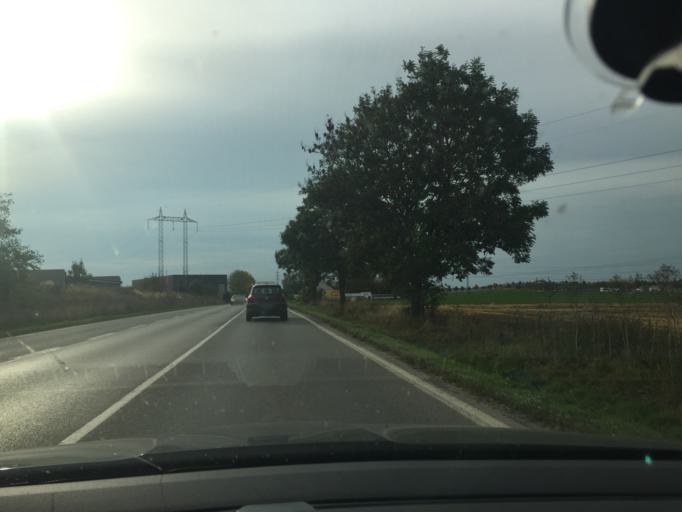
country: CZ
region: Central Bohemia
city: Sestajovice
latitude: 50.1240
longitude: 14.6825
